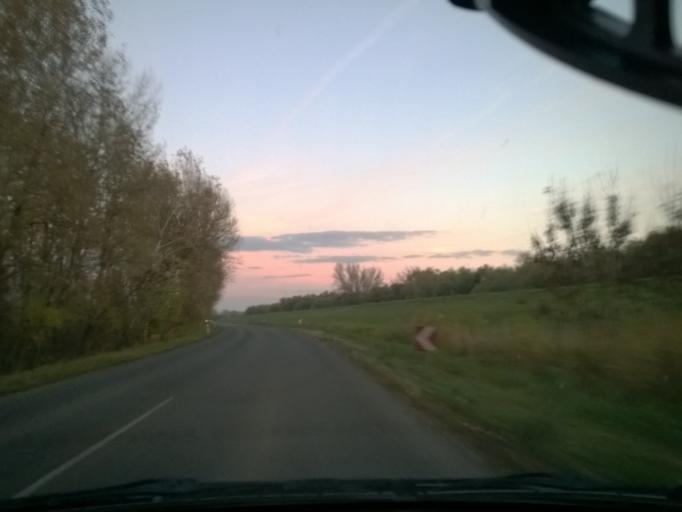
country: HU
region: Csongrad
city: Szentes
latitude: 46.6830
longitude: 20.2129
